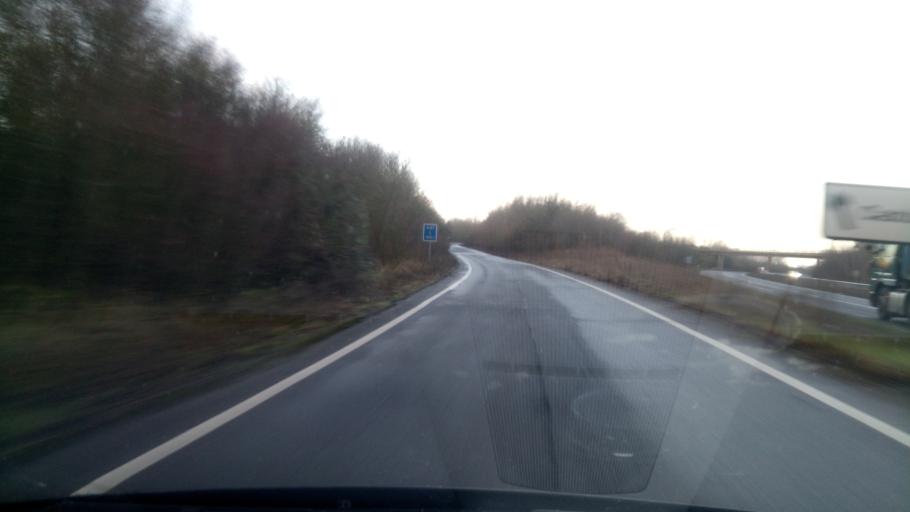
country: GB
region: England
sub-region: Peterborough
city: Castor
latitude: 52.5715
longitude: -0.3229
